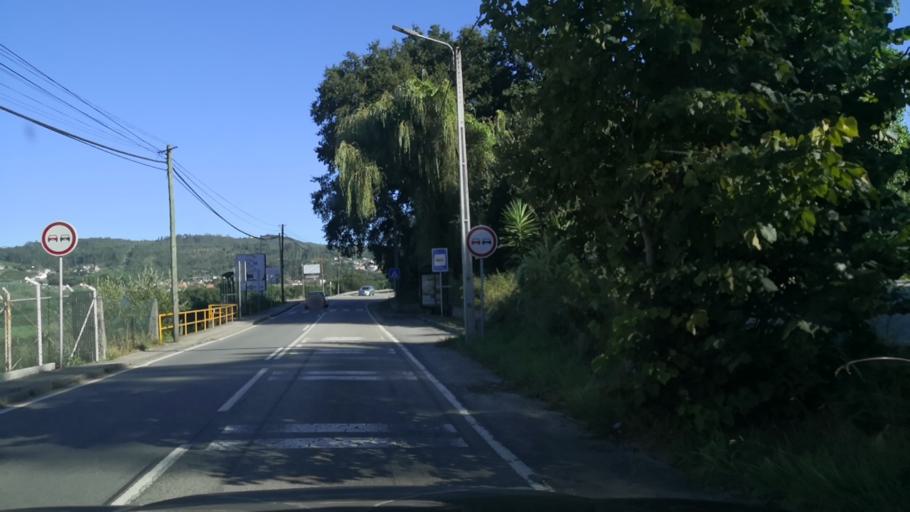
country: PT
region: Porto
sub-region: Pacos de Ferreira
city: Seroa
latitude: 41.2836
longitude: -8.4709
